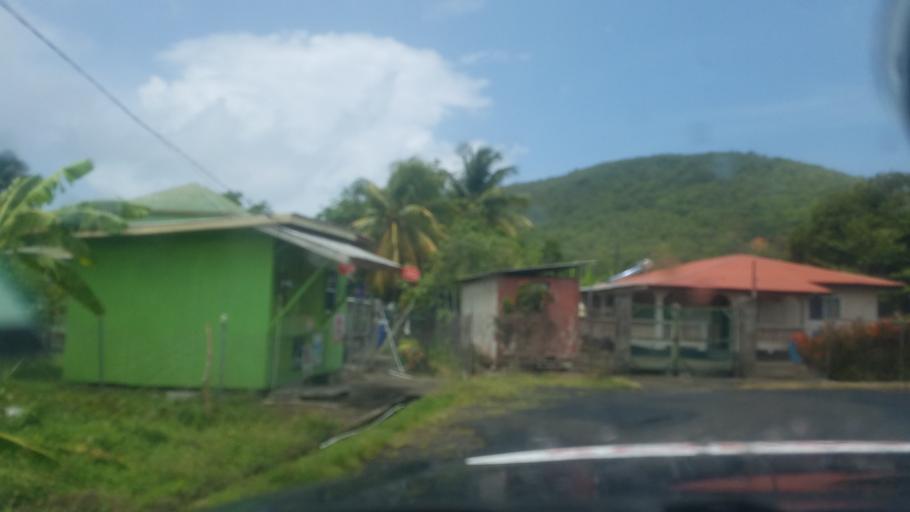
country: LC
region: Laborie Quarter
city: Laborie
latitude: 13.7466
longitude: -60.9618
